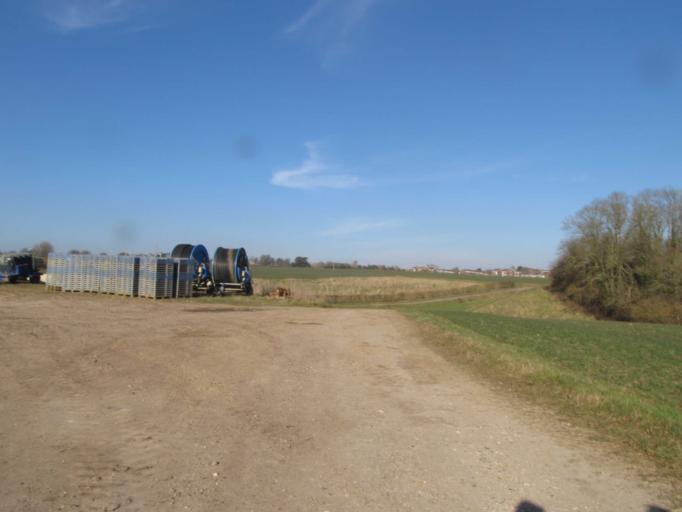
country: GB
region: England
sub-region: West Sussex
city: Petworth
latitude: 50.9786
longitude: -0.6198
